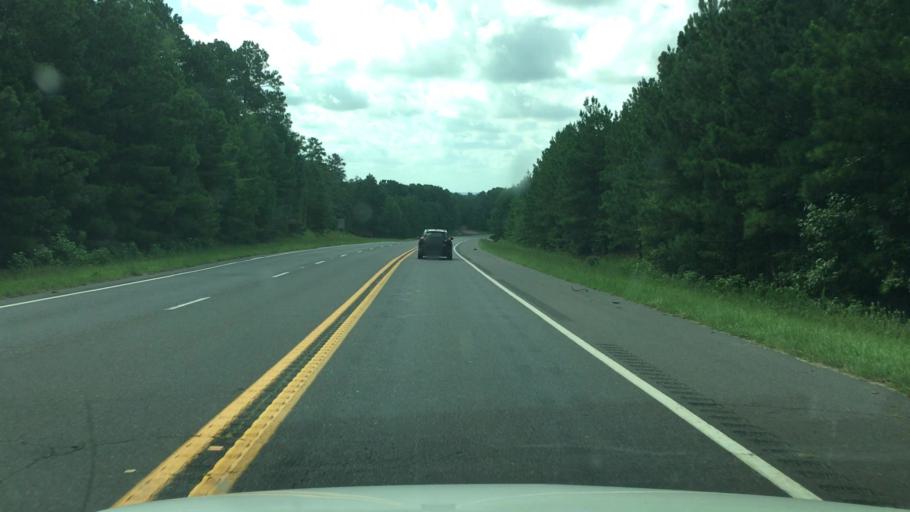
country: US
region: Arkansas
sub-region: Clark County
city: Arkadelphia
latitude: 34.2126
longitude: -93.0821
